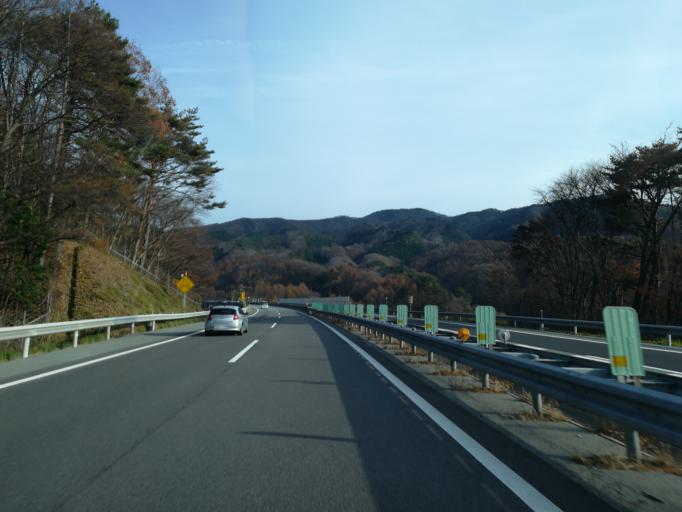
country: JP
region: Nagano
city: Saku
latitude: 36.2682
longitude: 138.5685
